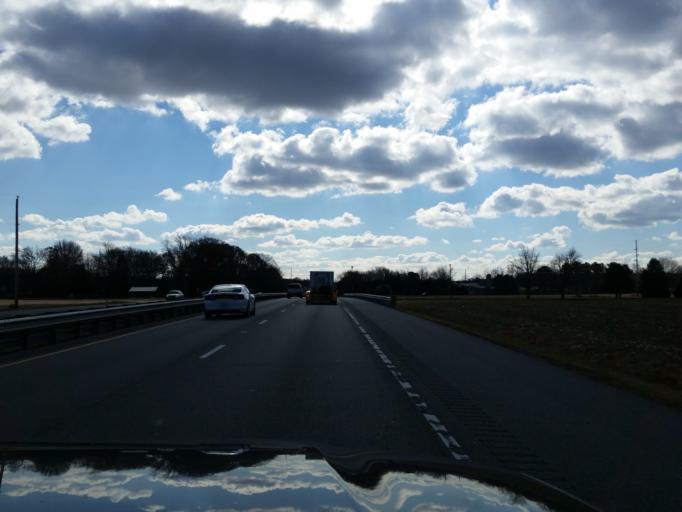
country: US
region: Maryland
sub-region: Talbot County
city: Easton
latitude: 38.8453
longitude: -76.0608
